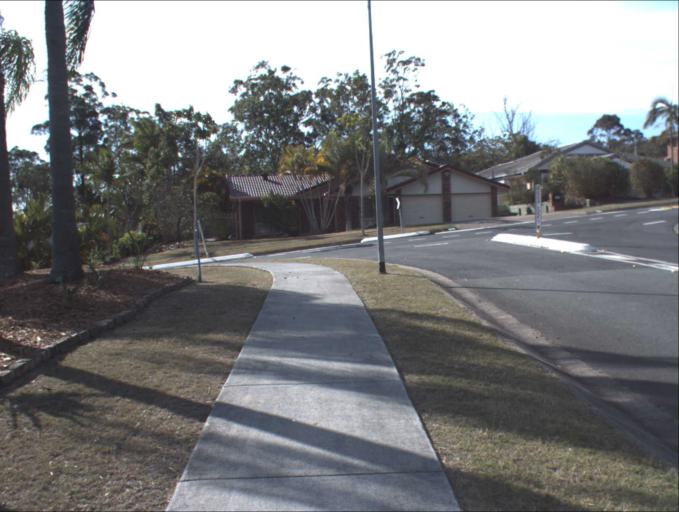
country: AU
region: Queensland
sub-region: Logan
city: Slacks Creek
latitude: -27.6402
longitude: 153.1782
